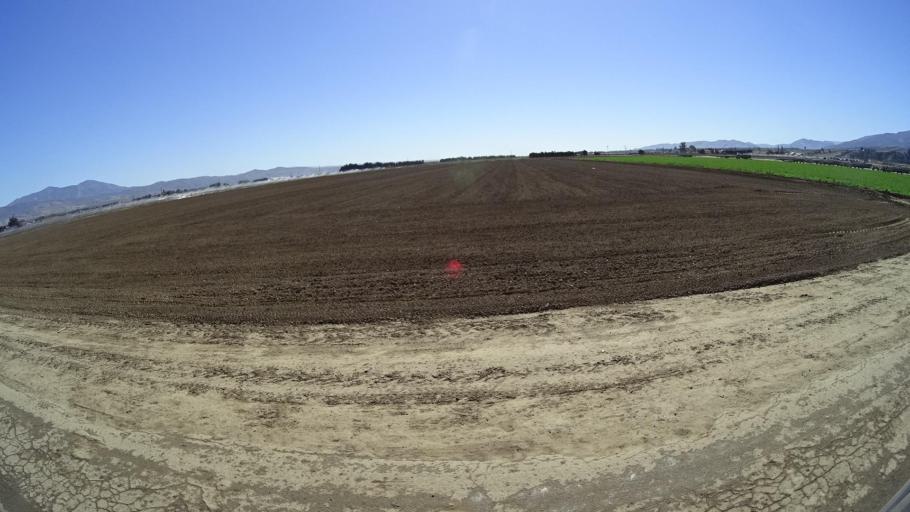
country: US
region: California
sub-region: Monterey County
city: Soledad
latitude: 36.3958
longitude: -121.3446
